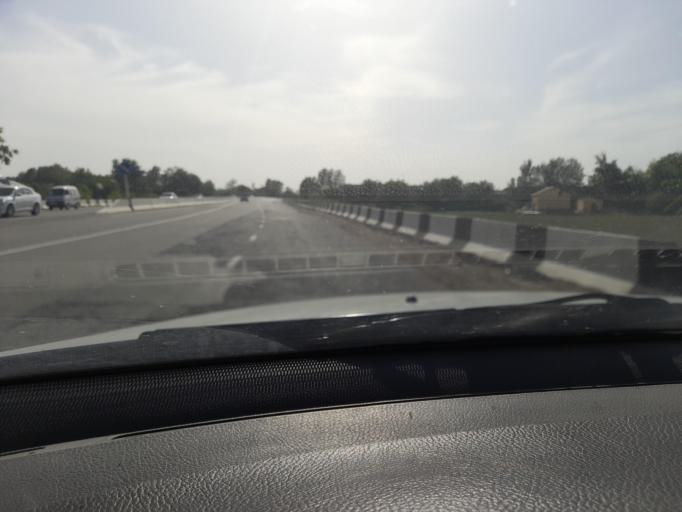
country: UZ
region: Samarqand
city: Kattaqo'rg'on
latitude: 39.9164
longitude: 66.3229
